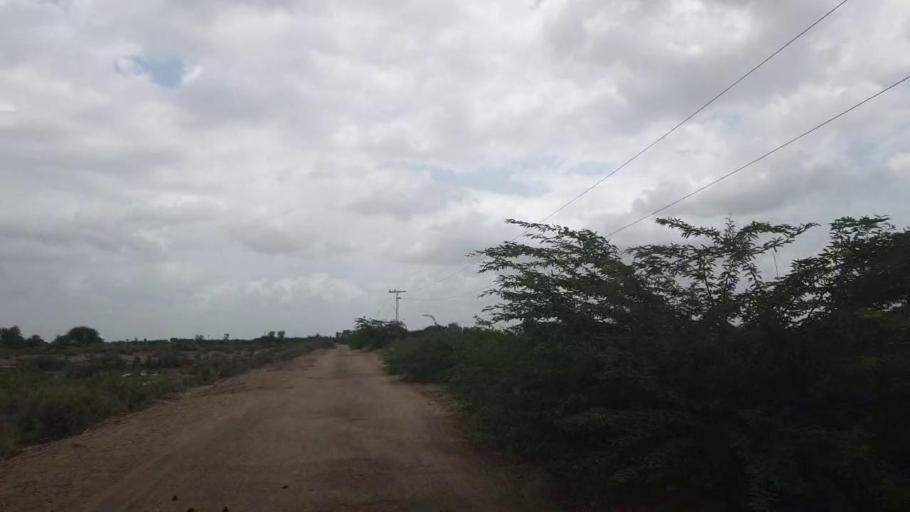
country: PK
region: Sindh
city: Badin
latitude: 24.6500
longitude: 68.9458
